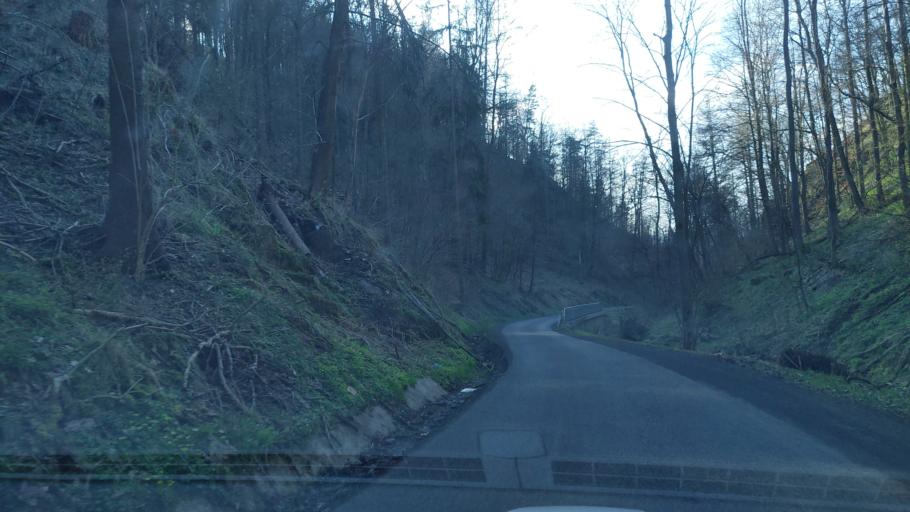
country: CZ
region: Ustecky
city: Vernerice
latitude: 50.7021
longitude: 14.2339
